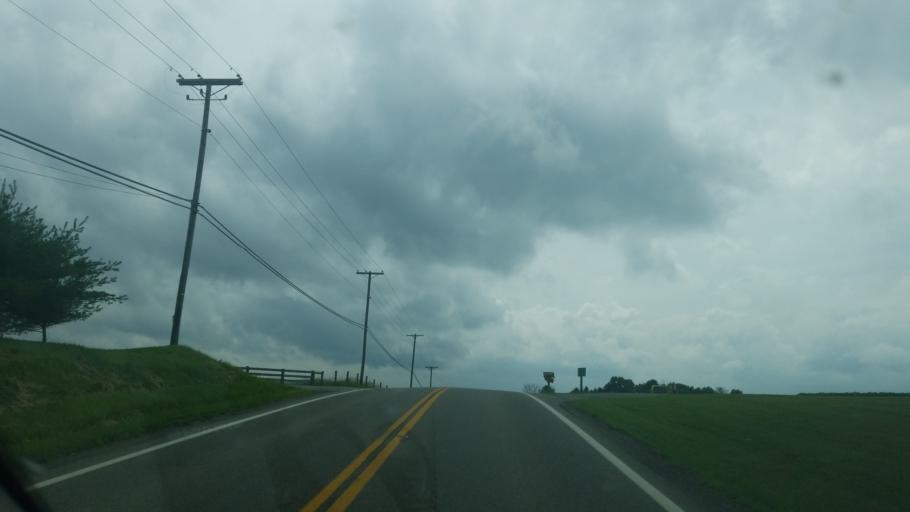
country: US
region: Ohio
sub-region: Holmes County
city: Millersburg
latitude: 40.5945
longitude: -81.8681
